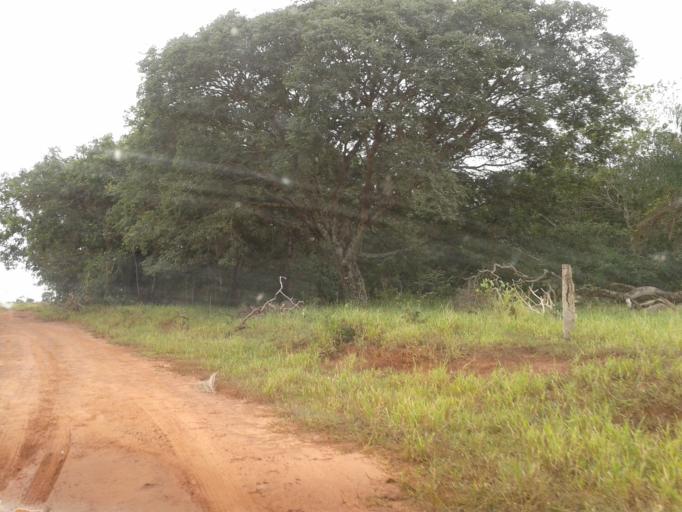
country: BR
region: Minas Gerais
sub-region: Campina Verde
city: Campina Verde
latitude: -19.5111
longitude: -49.6617
